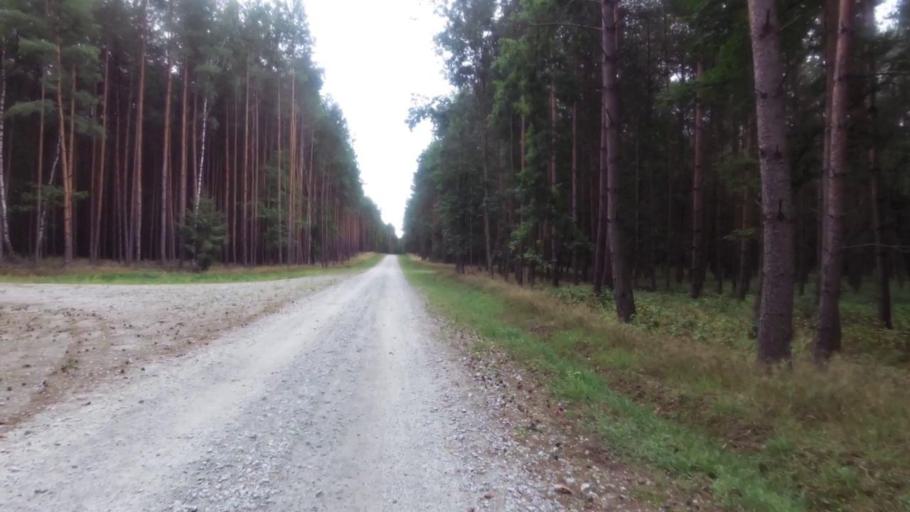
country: PL
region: West Pomeranian Voivodeship
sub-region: Powiat mysliborski
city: Boleszkowice
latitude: 52.6633
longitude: 14.6216
